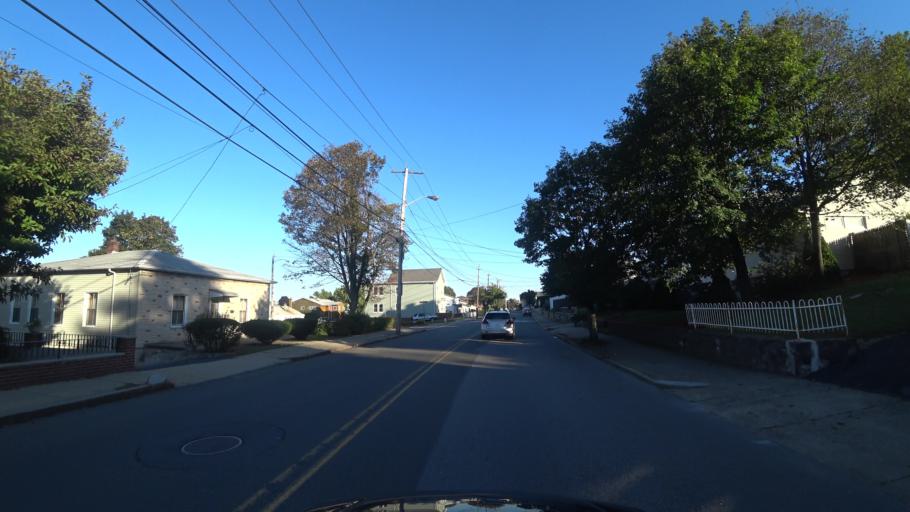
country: US
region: Massachusetts
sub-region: Suffolk County
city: Revere
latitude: 42.4192
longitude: -71.0124
